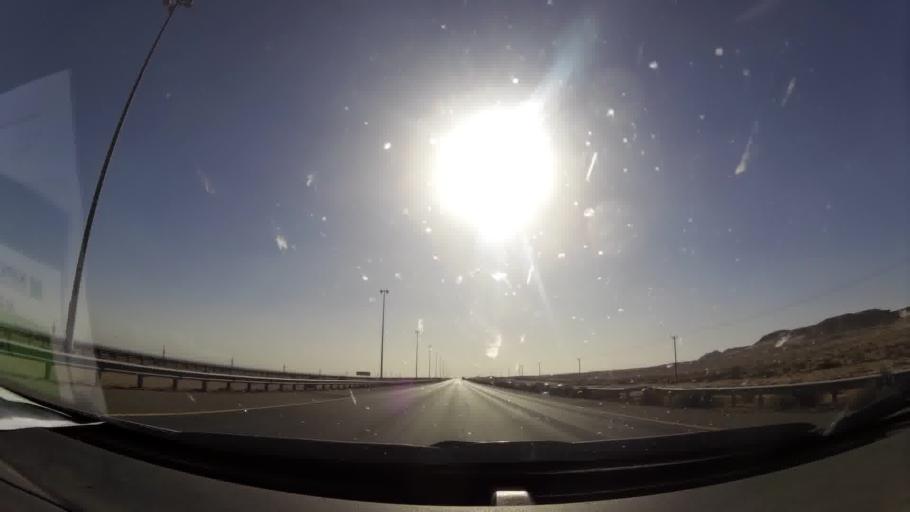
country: KW
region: Muhafazat al Jahra'
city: Al Jahra'
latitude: 29.5052
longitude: 47.7975
